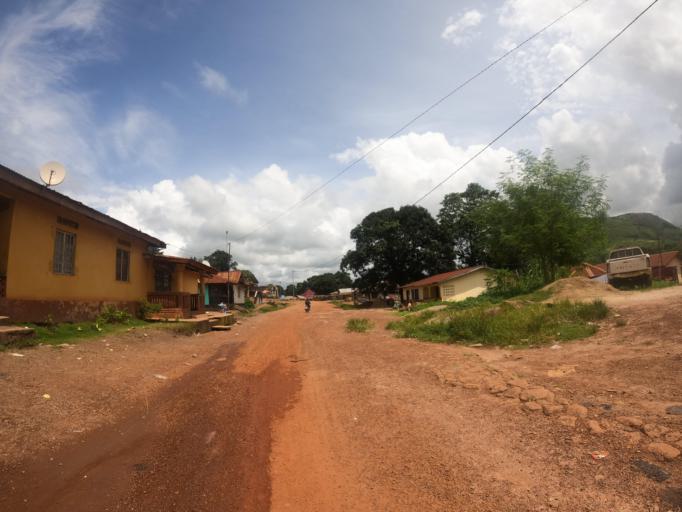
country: SL
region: Northern Province
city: Makeni
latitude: 8.8926
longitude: -12.0548
